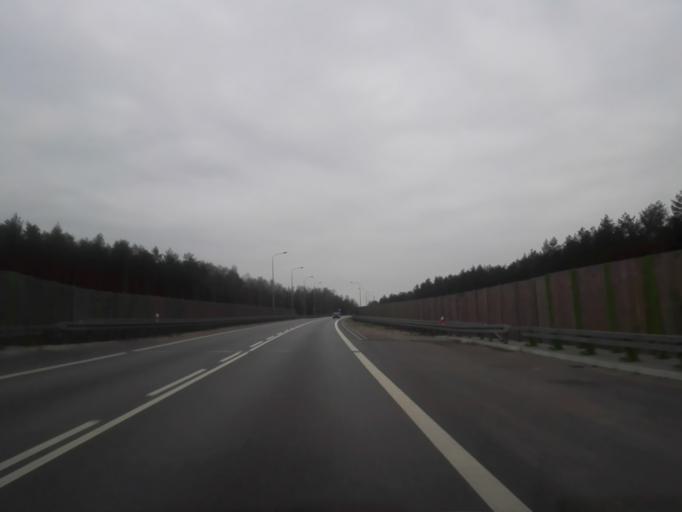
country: PL
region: Podlasie
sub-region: Powiat kolnenski
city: Stawiski
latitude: 53.3559
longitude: 22.1610
